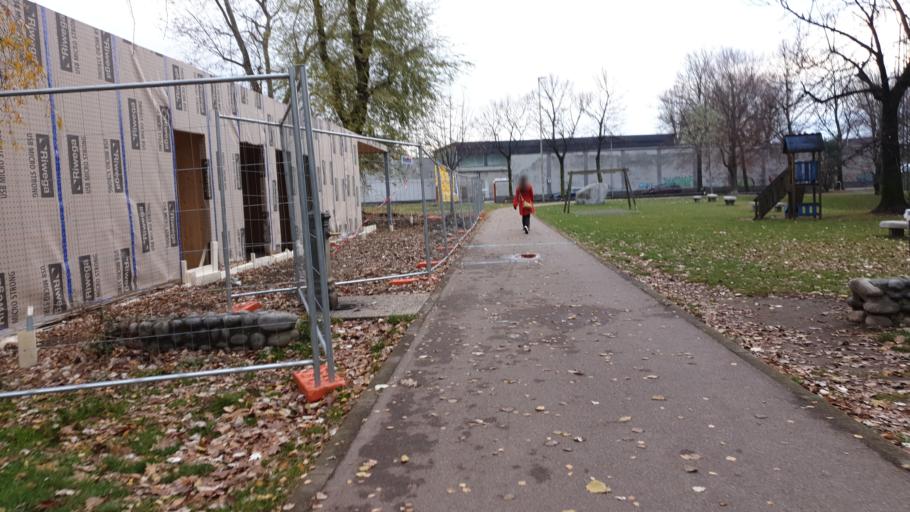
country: IT
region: Lombardy
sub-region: Provincia di Lecco
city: Pescate
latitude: 45.8413
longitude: 9.4002
